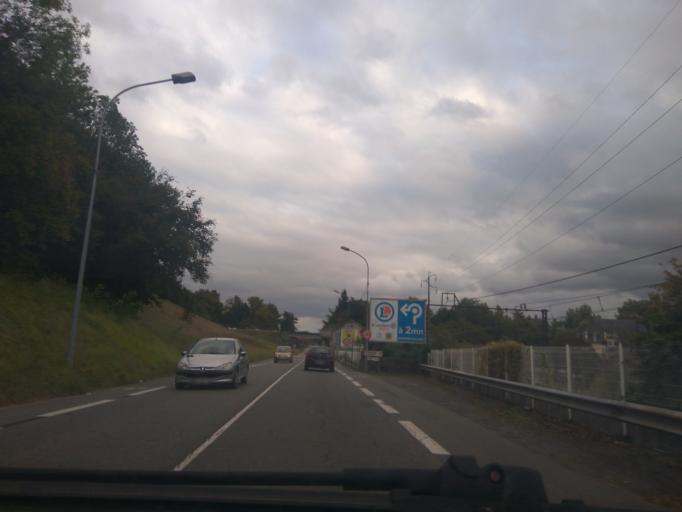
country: FR
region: Aquitaine
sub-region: Departement des Pyrenees-Atlantiques
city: Bizanos
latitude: 43.2865
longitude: -0.3497
